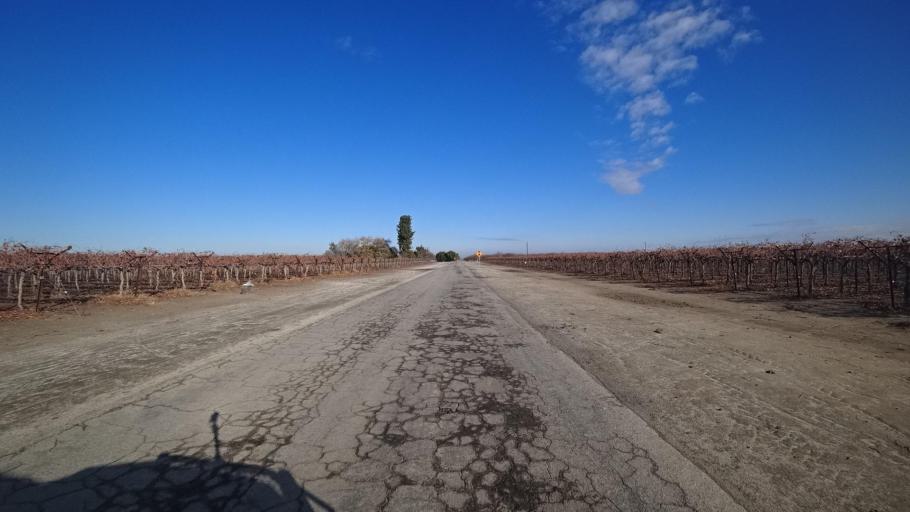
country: US
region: California
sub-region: Kern County
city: Delano
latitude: 35.7303
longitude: -119.3031
